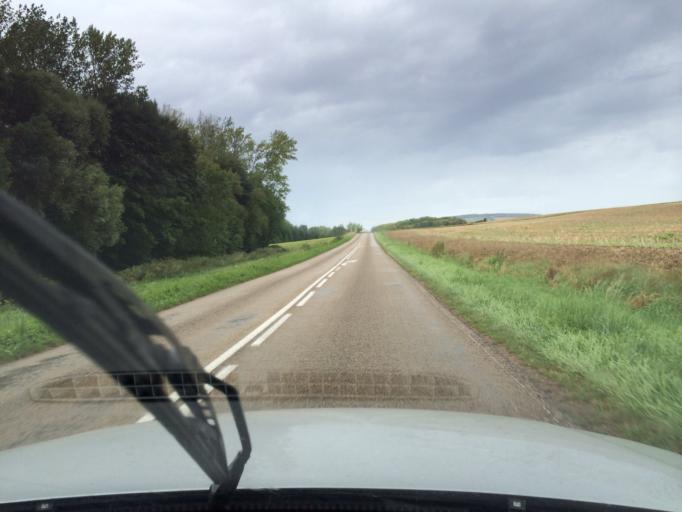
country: FR
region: Bourgogne
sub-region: Departement de l'Yonne
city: Aillant-sur-Tholon
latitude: 47.8946
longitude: 3.3548
